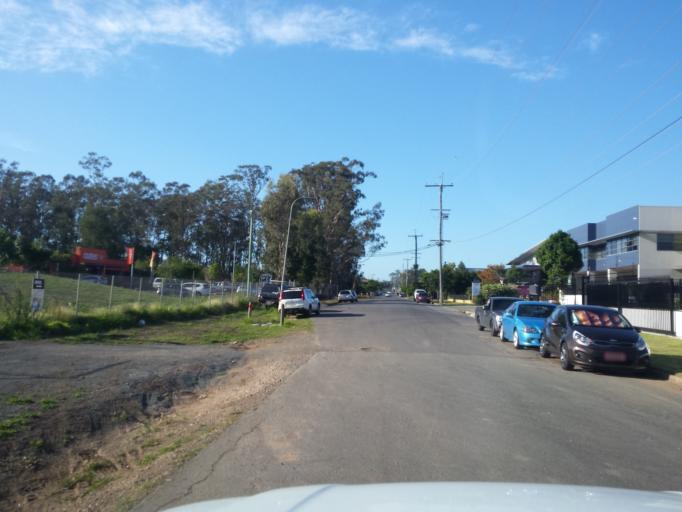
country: AU
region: Queensland
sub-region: Logan
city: Slacks Creek
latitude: -27.6589
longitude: 153.1340
